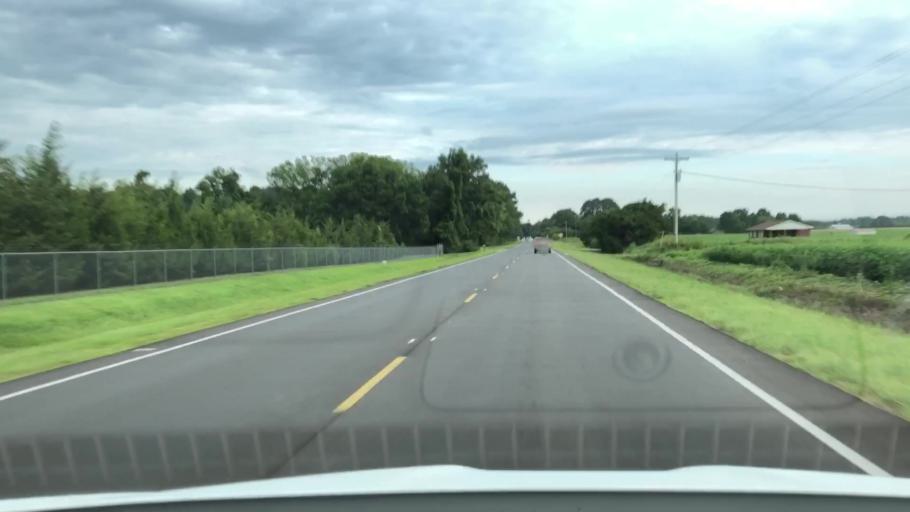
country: US
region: North Carolina
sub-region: Jones County
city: Maysville
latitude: 34.8946
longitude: -77.2180
